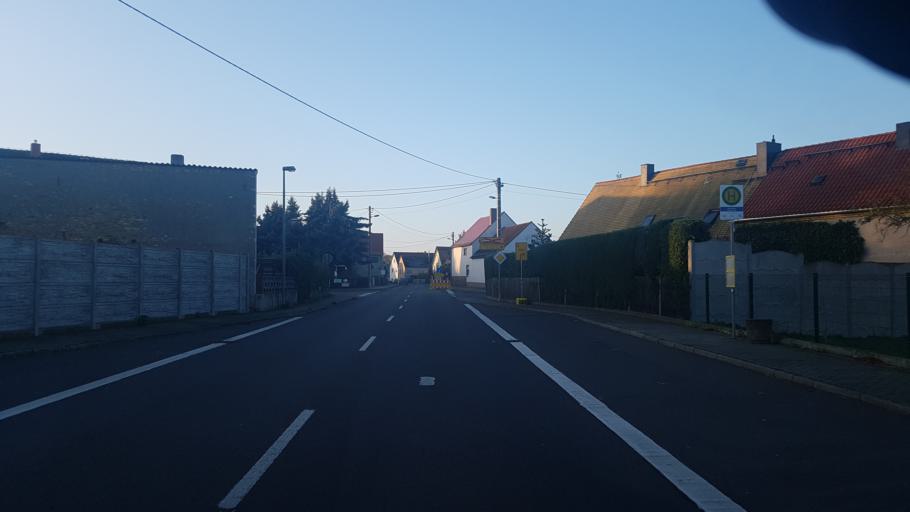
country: DE
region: Saxony
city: Schildau
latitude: 51.4515
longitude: 12.9712
